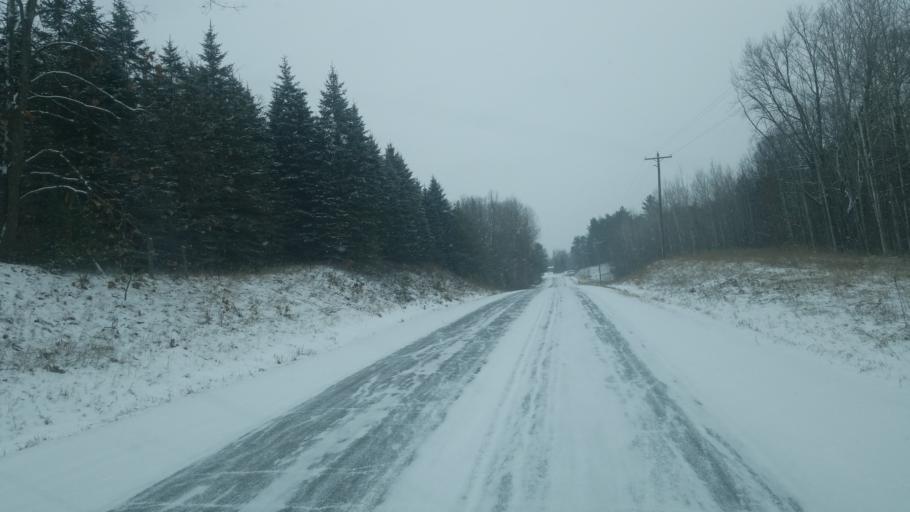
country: US
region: Michigan
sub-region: Osceola County
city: Reed City
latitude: 43.8037
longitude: -85.4023
